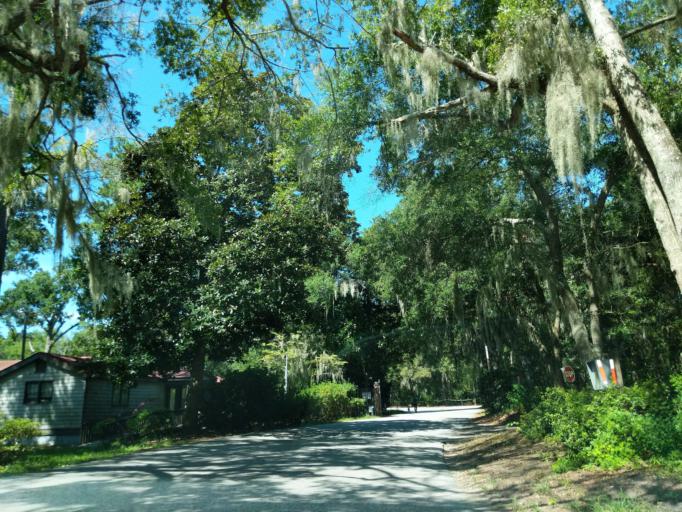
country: US
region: South Carolina
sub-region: Charleston County
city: Charleston
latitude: 32.7484
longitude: -79.9045
